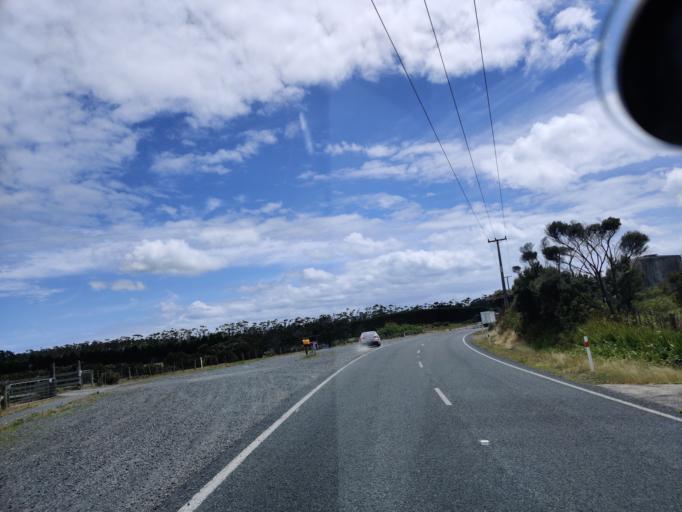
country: NZ
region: Northland
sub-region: Far North District
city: Kaitaia
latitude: -34.8289
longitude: 173.1279
